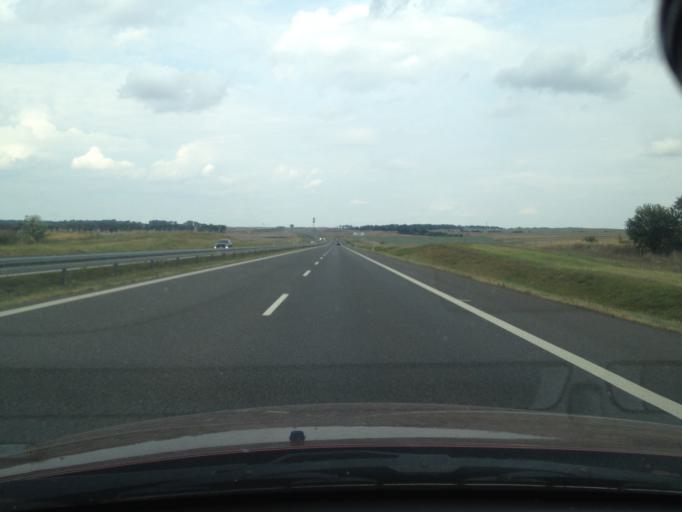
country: PL
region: West Pomeranian Voivodeship
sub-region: Powiat pyrzycki
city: Kozielice
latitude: 53.0350
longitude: 14.8645
